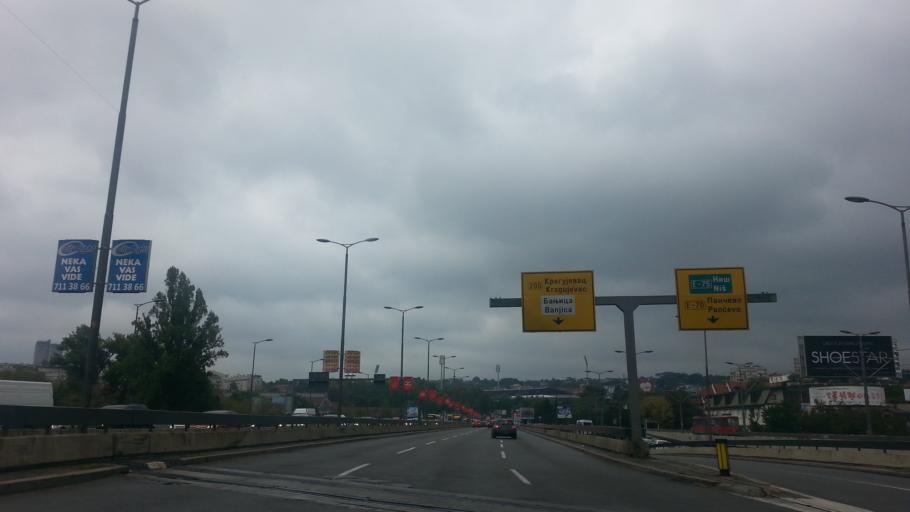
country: RS
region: Central Serbia
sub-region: Belgrade
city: Vracar
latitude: 44.7930
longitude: 20.4663
